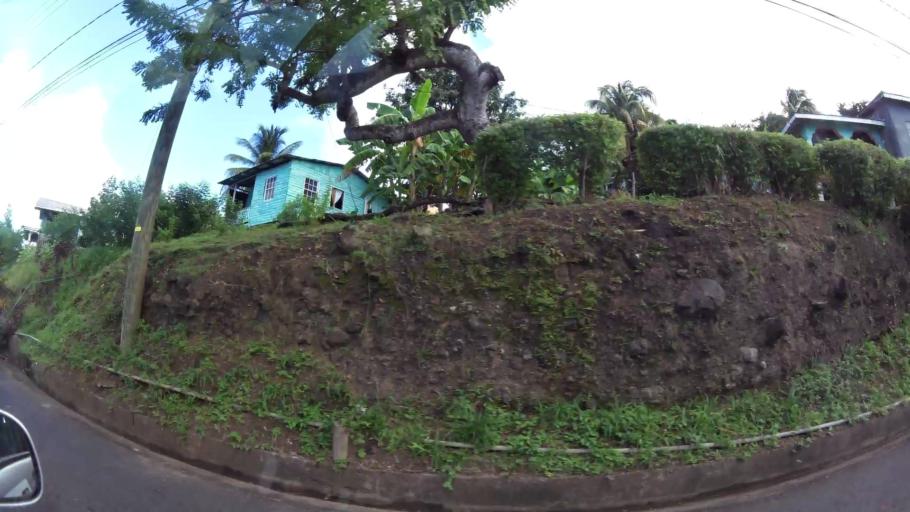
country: GD
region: Saint Mark
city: Victoria
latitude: 12.2067
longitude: -61.6978
